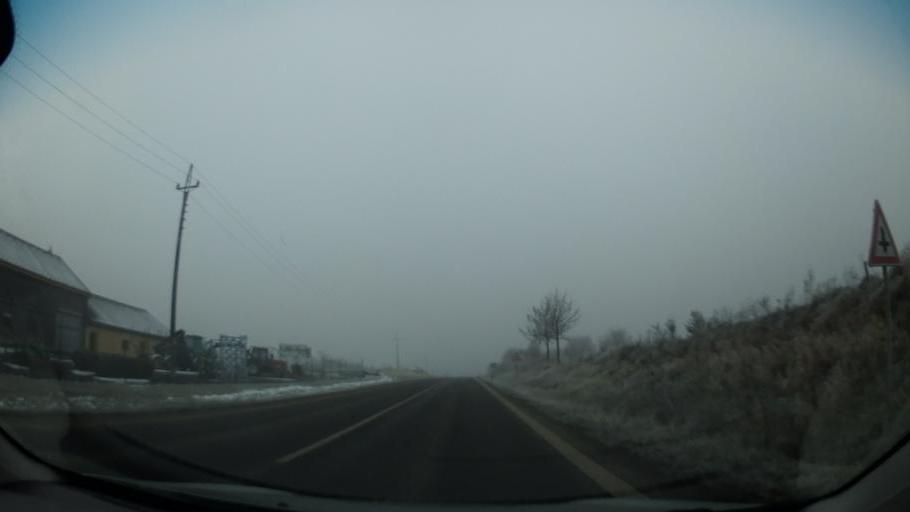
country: CZ
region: Vysocina
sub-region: Okres Trebic
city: Trebic
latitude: 49.2629
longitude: 15.9292
